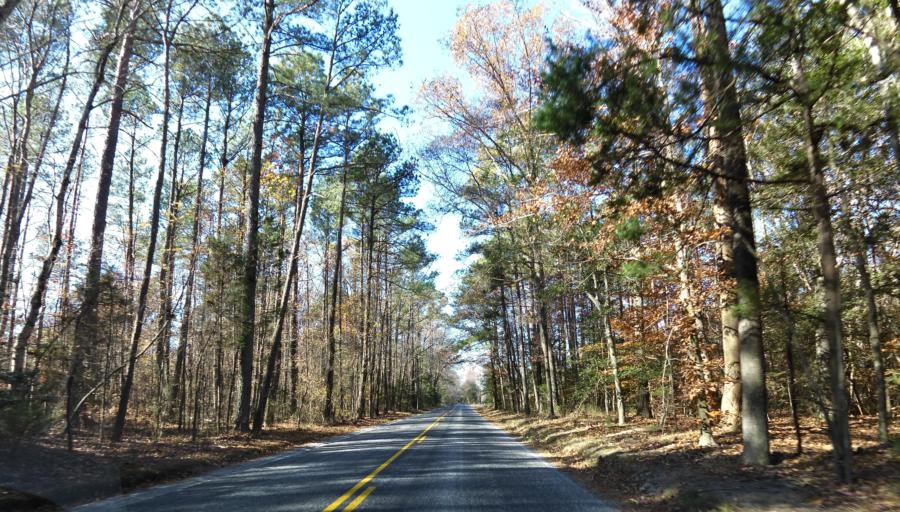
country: US
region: Virginia
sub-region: Hanover County
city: Hanover
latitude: 37.7156
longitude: -77.4161
